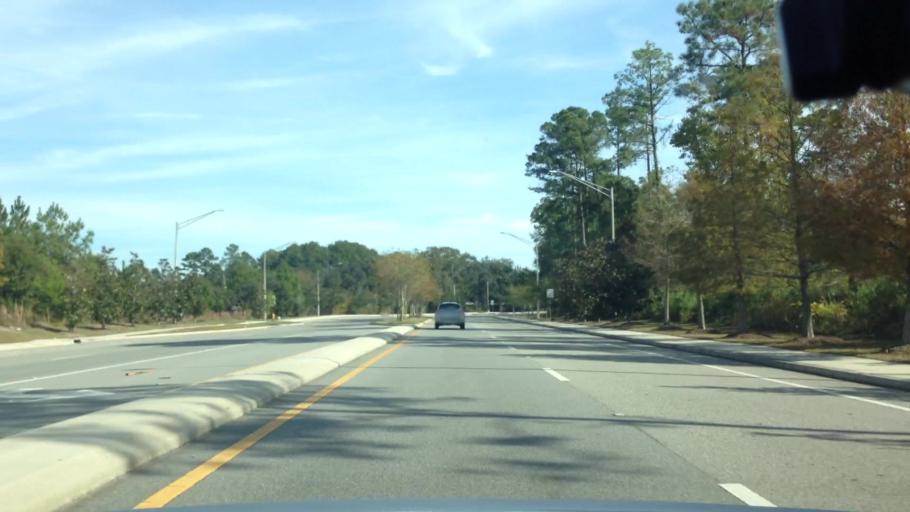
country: US
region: Florida
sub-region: Nassau County
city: Yulee
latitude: 30.4906
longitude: -81.6287
